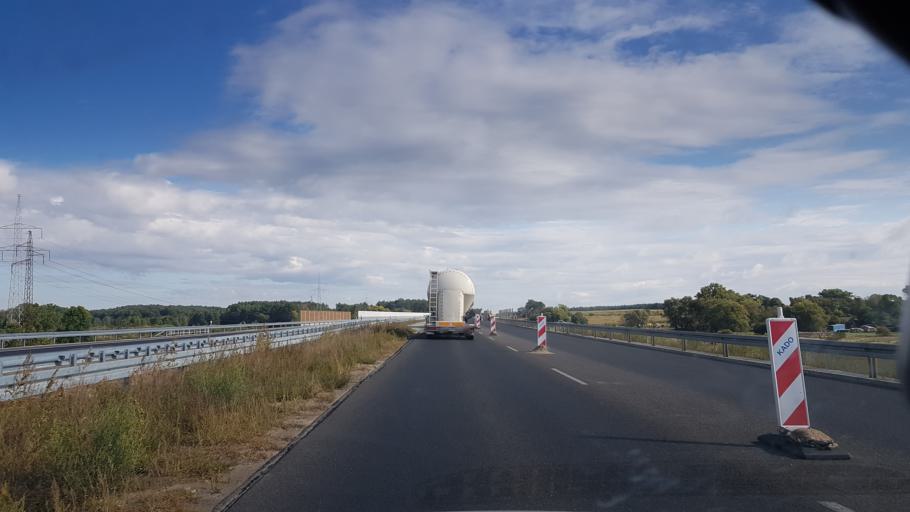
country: PL
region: Greater Poland Voivodeship
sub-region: Powiat poznanski
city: Steszew
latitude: 52.2902
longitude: 16.6788
